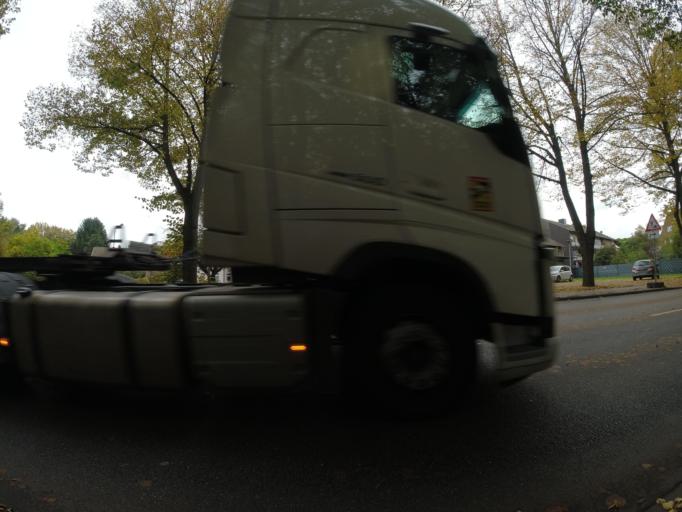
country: DE
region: North Rhine-Westphalia
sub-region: Regierungsbezirk Dusseldorf
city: Hochfeld
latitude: 51.4134
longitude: 6.6981
